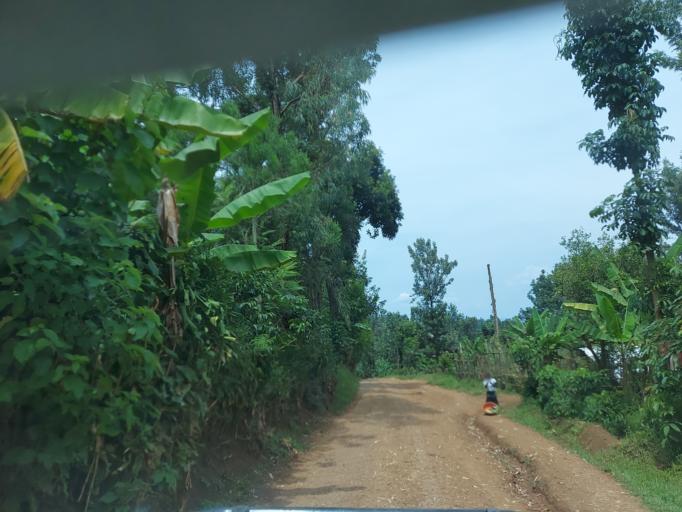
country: CD
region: South Kivu
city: Bukavu
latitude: -2.2360
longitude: 28.8474
